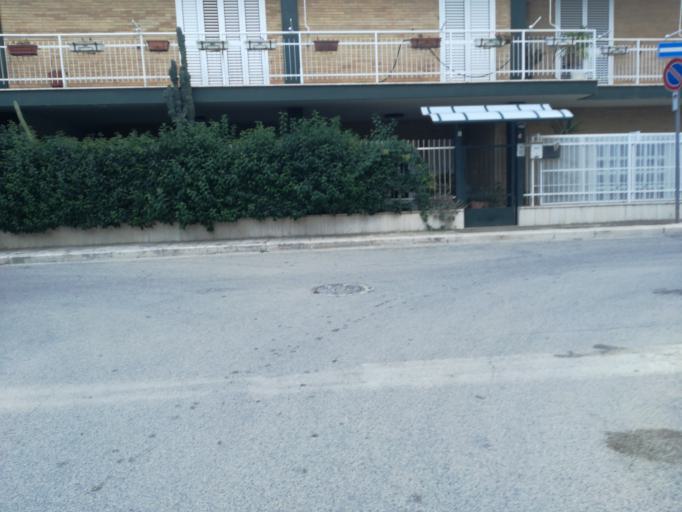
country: IT
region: Apulia
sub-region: Provincia di Bari
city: Triggiano
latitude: 41.0683
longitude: 16.9357
